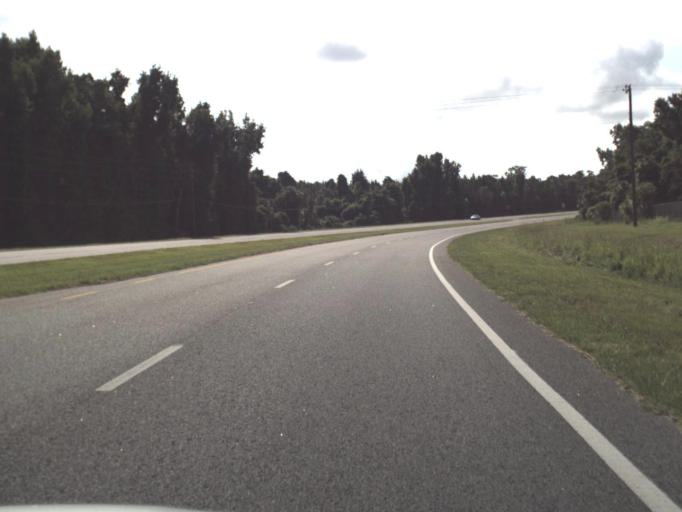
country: US
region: Florida
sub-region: Alachua County
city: Gainesville
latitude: 29.5099
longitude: -82.2738
